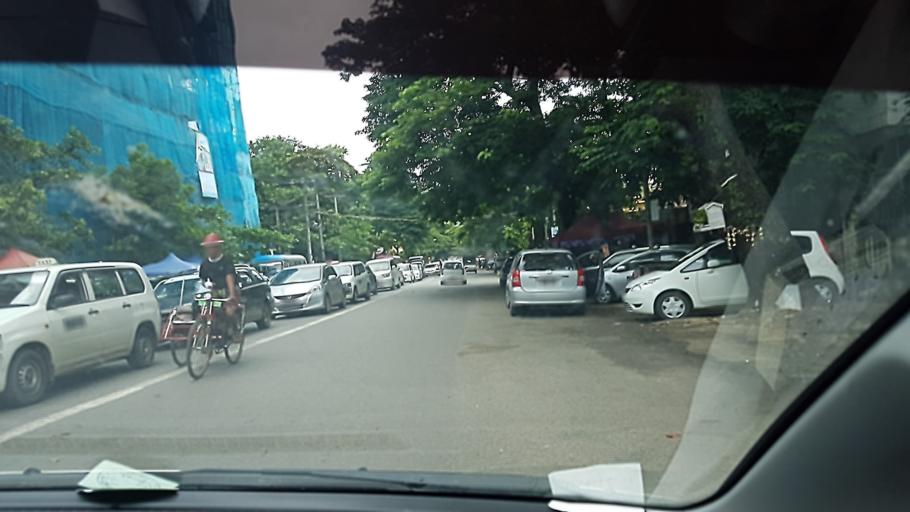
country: MM
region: Yangon
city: Yangon
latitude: 16.8054
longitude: 96.1296
